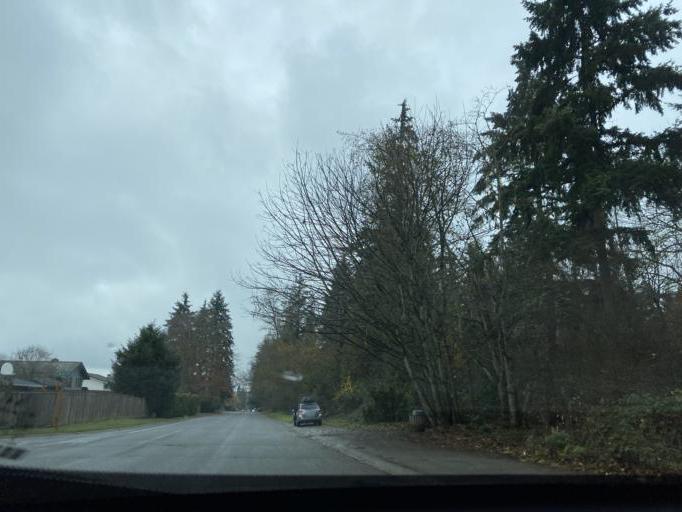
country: US
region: Washington
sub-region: King County
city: Mercer Island
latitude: 47.5433
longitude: -122.2270
